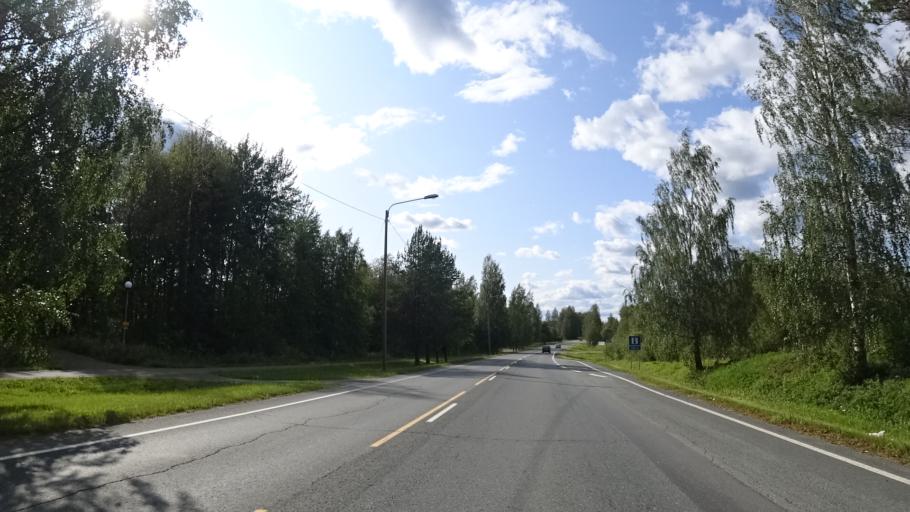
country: FI
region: North Karelia
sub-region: Keski-Karjala
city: Tohmajaervi
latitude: 62.2227
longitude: 30.3473
